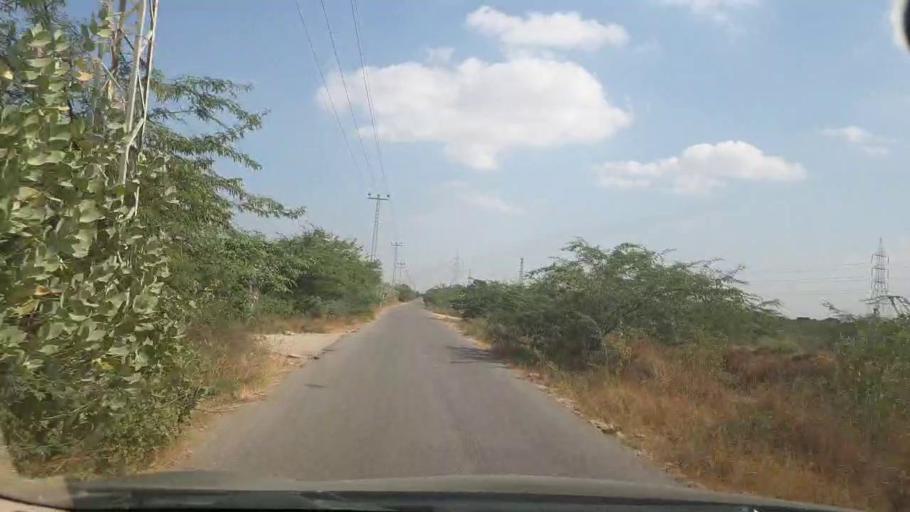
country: PK
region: Sindh
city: Malir Cantonment
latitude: 25.0185
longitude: 67.3604
